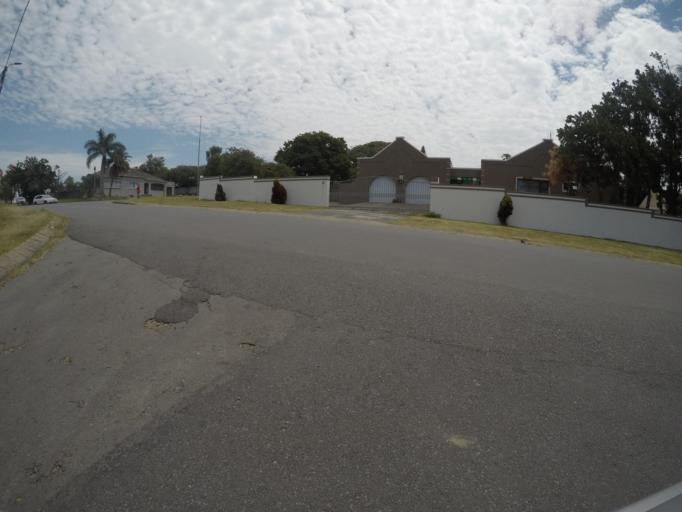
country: ZA
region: Eastern Cape
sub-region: Buffalo City Metropolitan Municipality
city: East London
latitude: -32.9850
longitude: 27.8617
